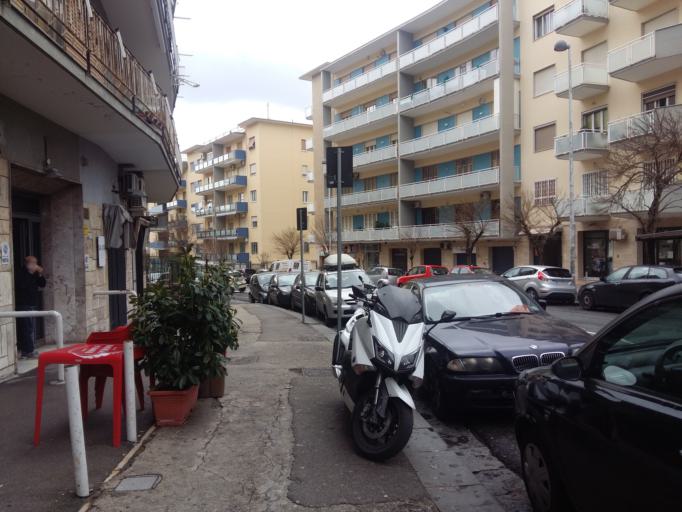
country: IT
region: Campania
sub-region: Provincia di Napoli
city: Napoli
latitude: 40.8581
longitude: 14.2278
